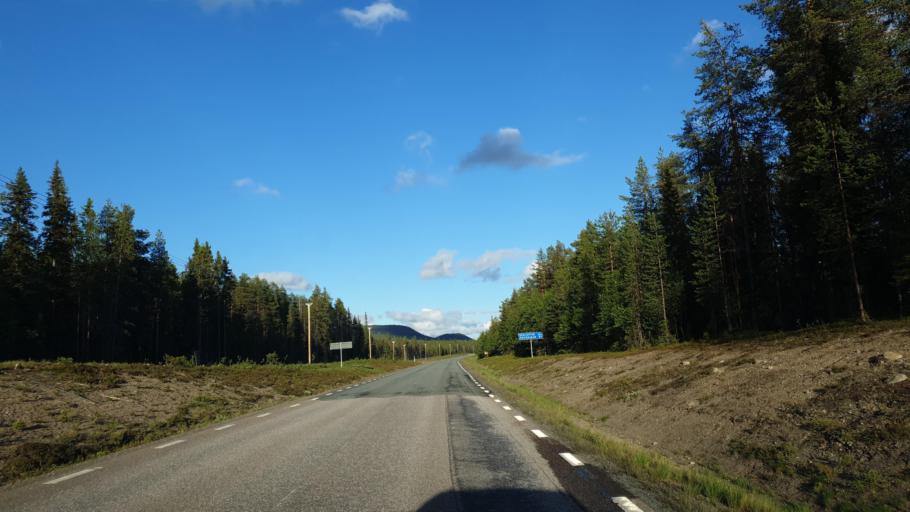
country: SE
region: Norrbotten
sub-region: Arvidsjaurs Kommun
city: Arvidsjaur
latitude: 65.7266
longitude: 18.6710
